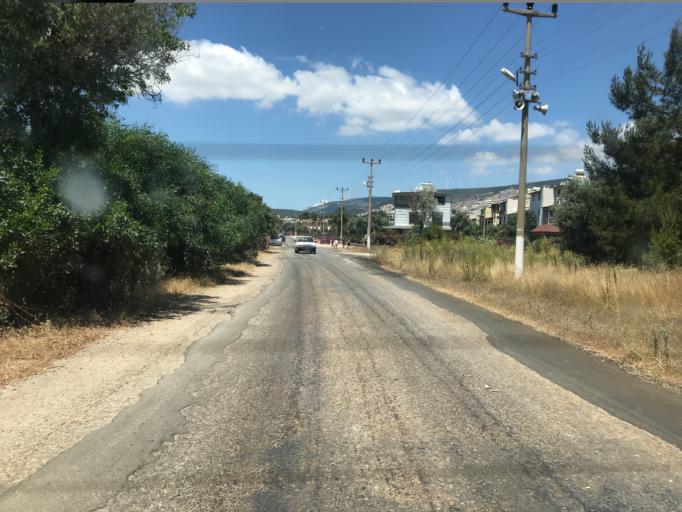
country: TR
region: Aydin
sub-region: Didim
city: Didim
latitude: 37.4028
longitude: 27.4315
